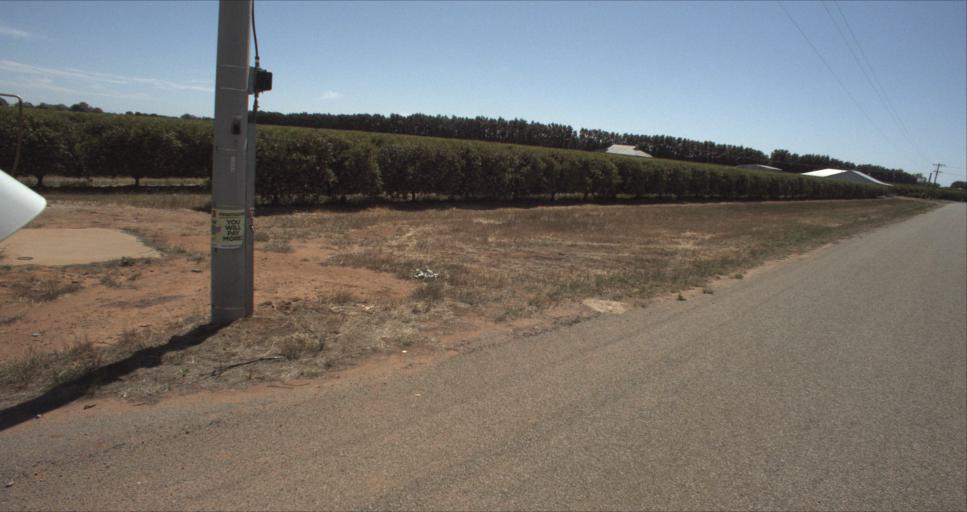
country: AU
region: New South Wales
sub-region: Leeton
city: Leeton
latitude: -34.5403
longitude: 146.3524
